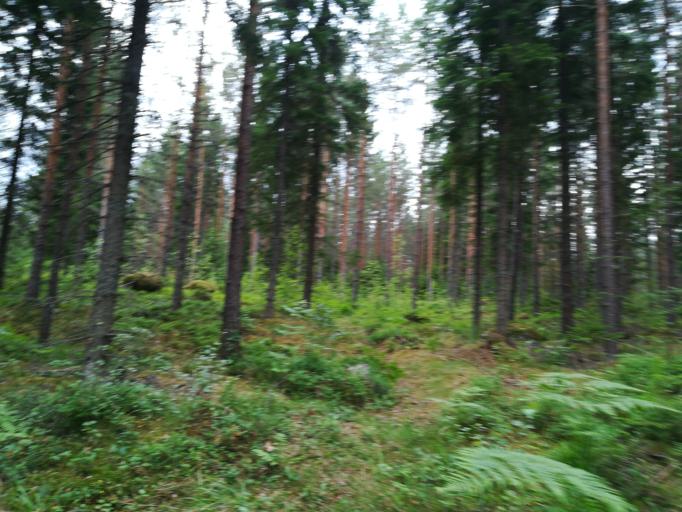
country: FI
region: South Karelia
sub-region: Lappeenranta
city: Savitaipale
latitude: 61.3030
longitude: 27.6181
